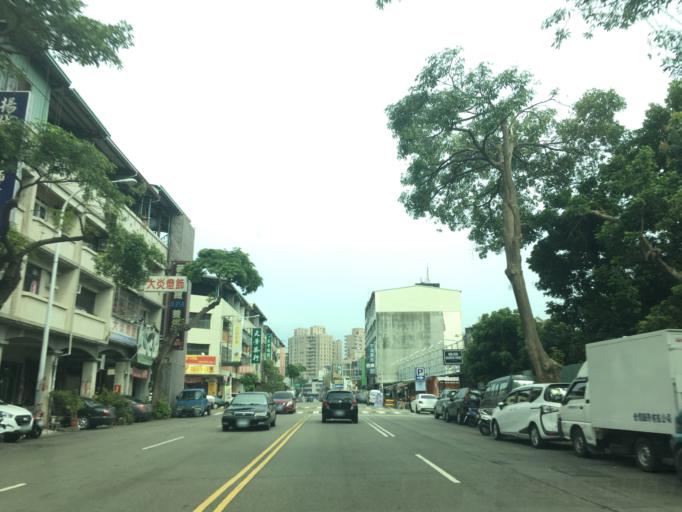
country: TW
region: Taiwan
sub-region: Taichung City
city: Taichung
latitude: 24.1669
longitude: 120.6870
